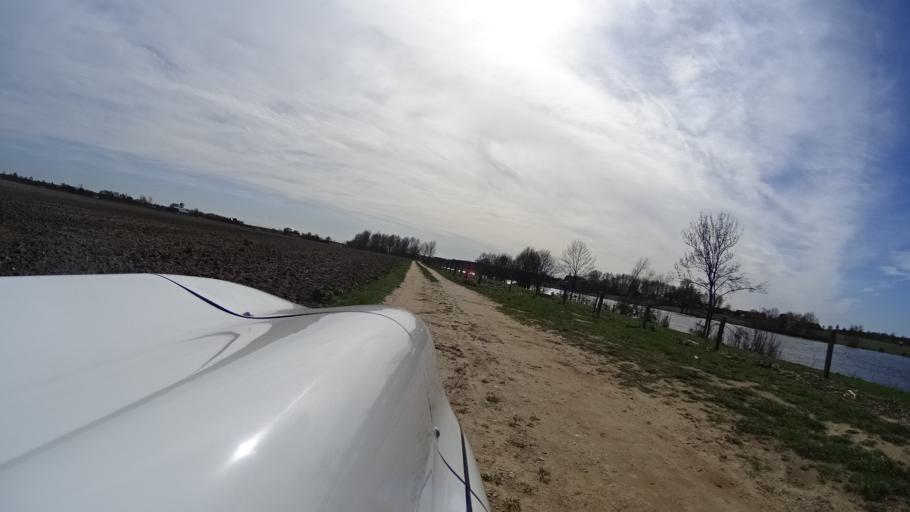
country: NL
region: Limburg
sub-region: Gemeente Venlo
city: Arcen
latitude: 51.4919
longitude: 6.1686
